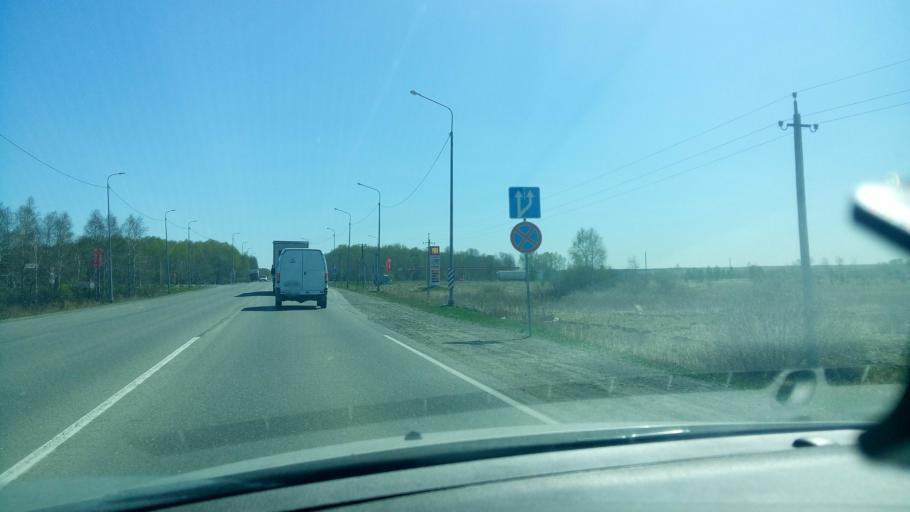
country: RU
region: Sverdlovsk
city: Bogdanovich
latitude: 56.7548
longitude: 62.1953
